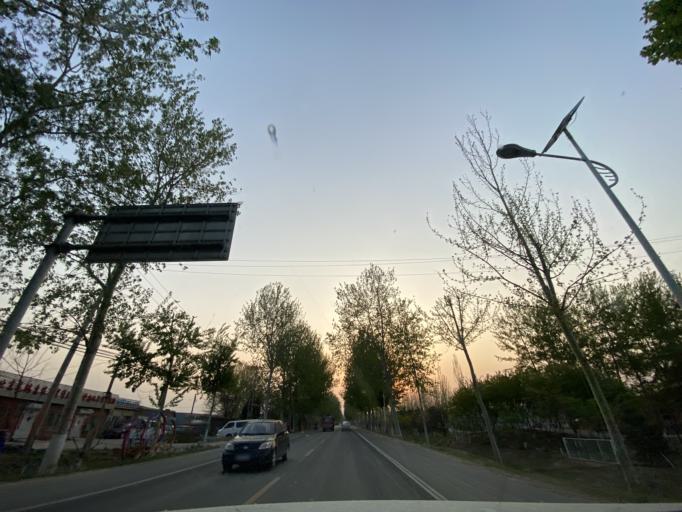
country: CN
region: Beijing
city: Weishanzhuang
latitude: 39.6152
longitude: 116.4038
